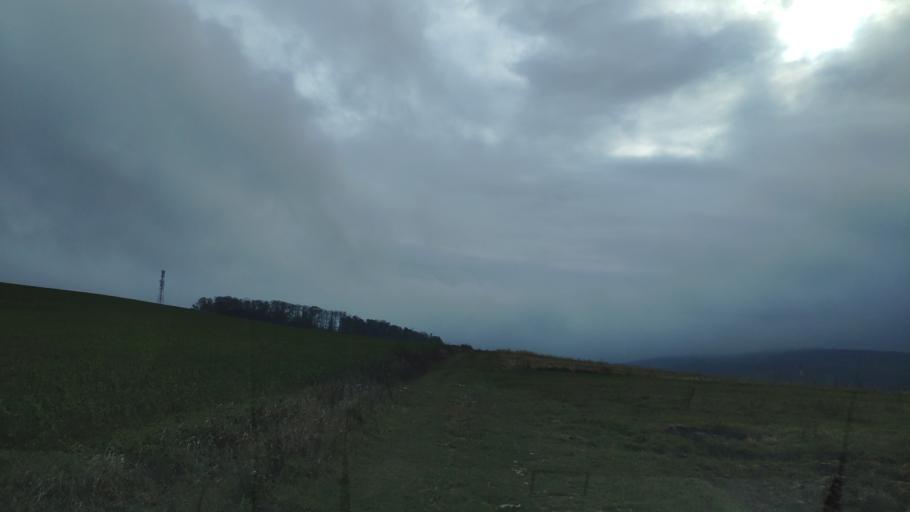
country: SK
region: Presovsky
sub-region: Okres Presov
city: Presov
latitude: 49.0073
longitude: 21.1923
